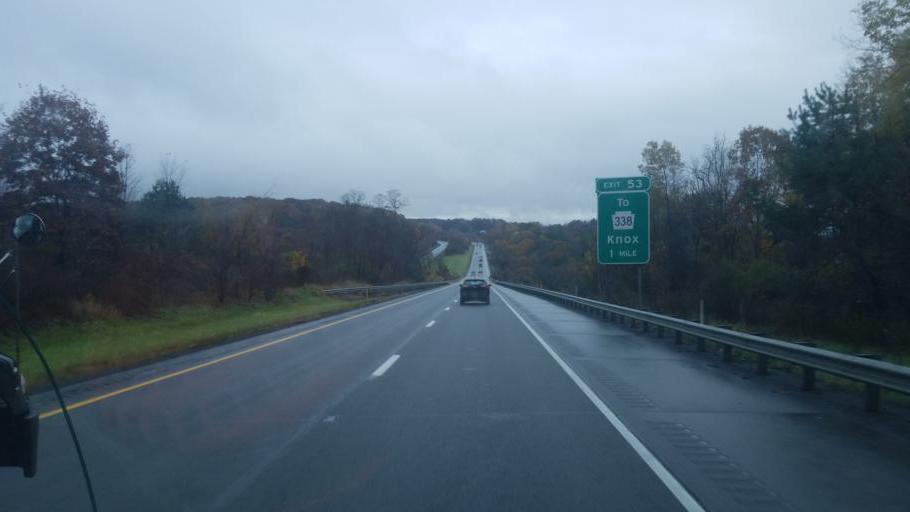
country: US
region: Pennsylvania
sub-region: Clarion County
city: Knox
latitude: 41.1911
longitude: -79.5652
